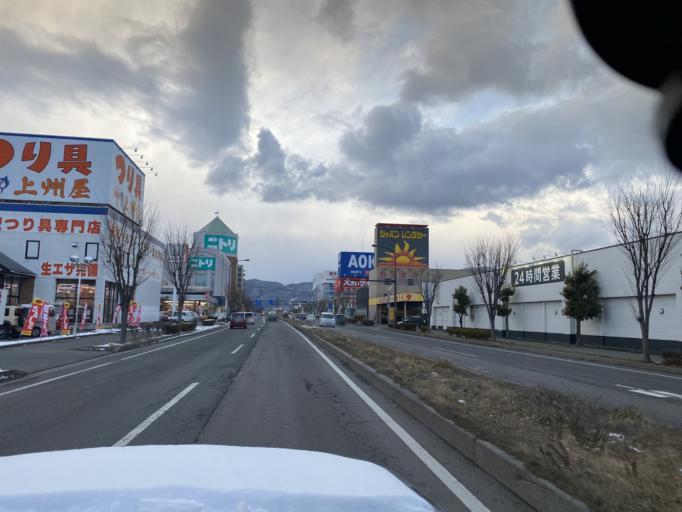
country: JP
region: Nagano
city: Nagano-shi
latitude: 36.6036
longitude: 138.1685
